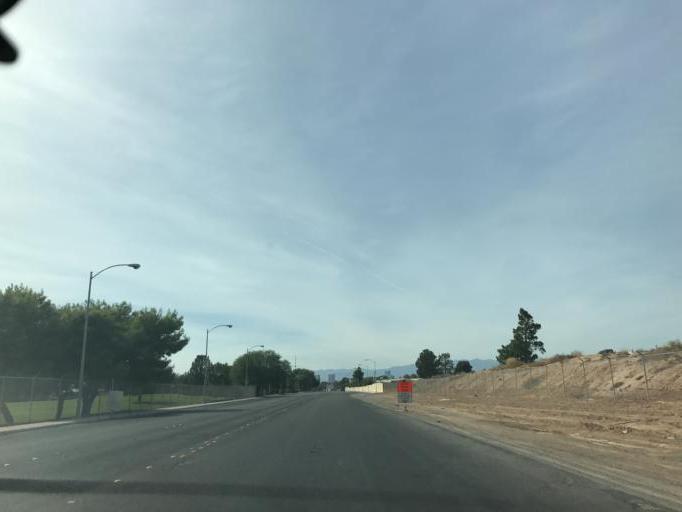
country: US
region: Nevada
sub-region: Clark County
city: Whitney
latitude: 36.1297
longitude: -115.0499
